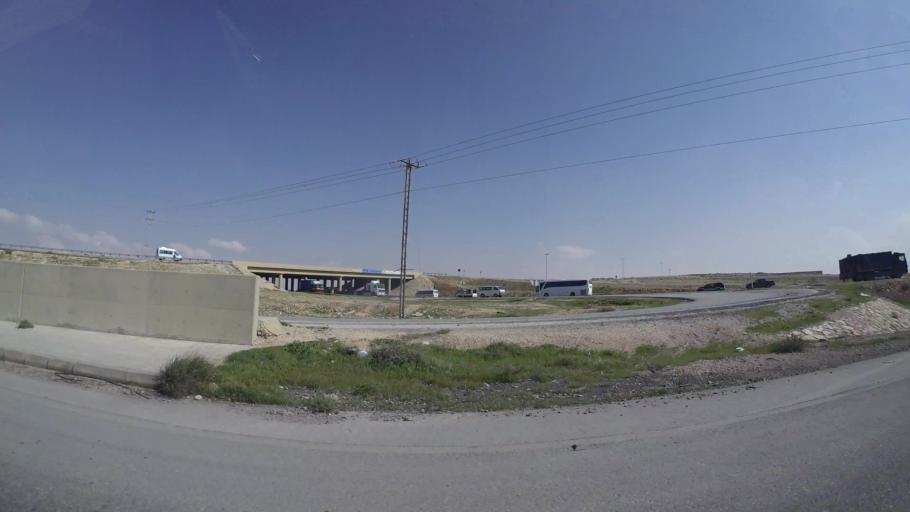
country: JO
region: Zarqa
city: Zarqa
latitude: 32.0515
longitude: 36.1314
